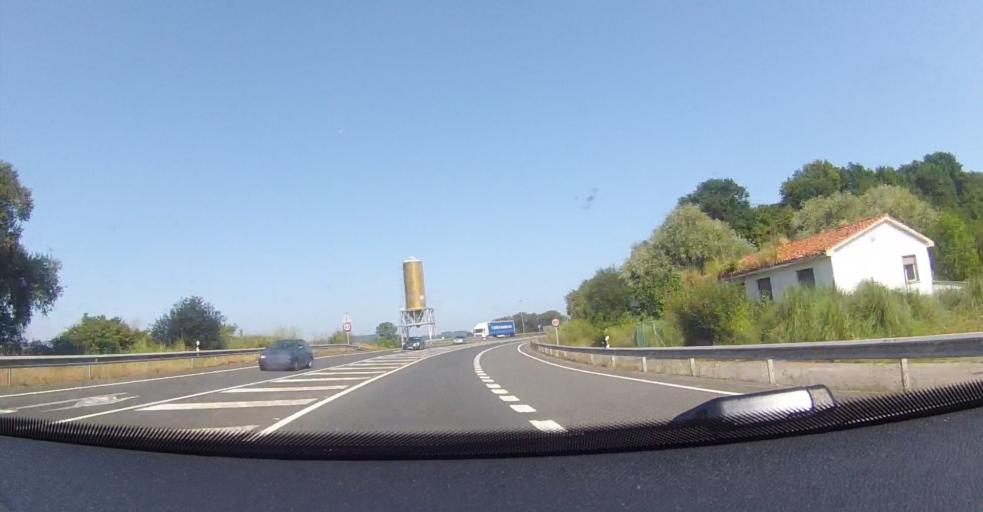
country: ES
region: Cantabria
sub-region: Provincia de Cantabria
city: Colindres
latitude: 43.3882
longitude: -3.4468
